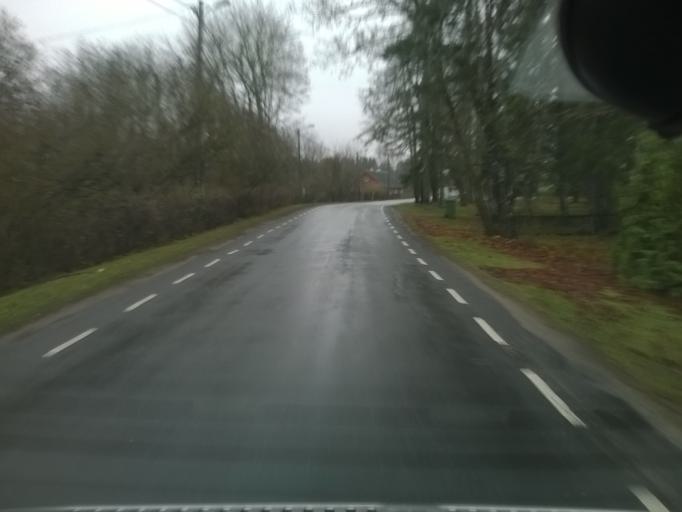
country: EE
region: Harju
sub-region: Nissi vald
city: Riisipere
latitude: 59.1190
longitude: 24.3080
